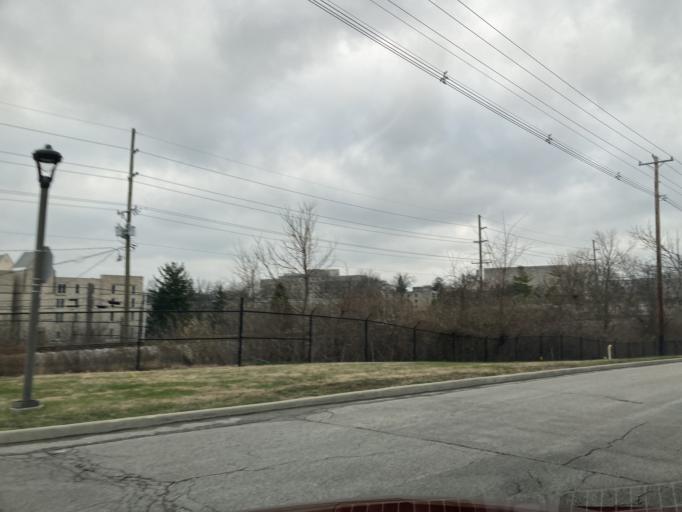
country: US
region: Indiana
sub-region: Monroe County
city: Bloomington
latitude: 39.1724
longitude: -86.5097
